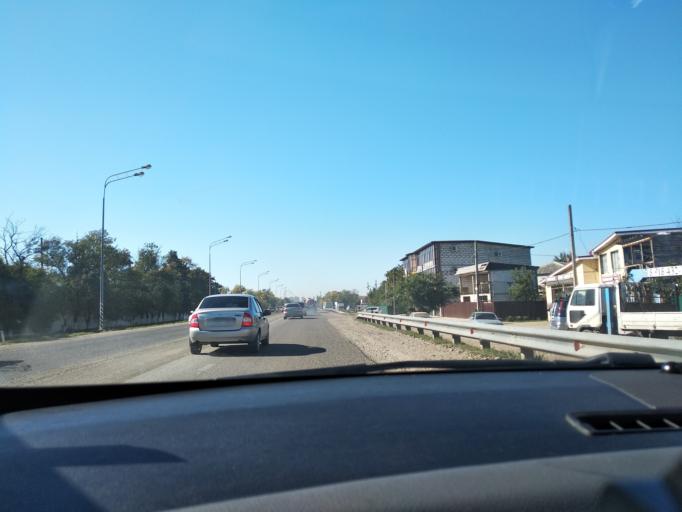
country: RU
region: Krasnodarskiy
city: Krasnodar
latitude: 45.1324
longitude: 39.0222
